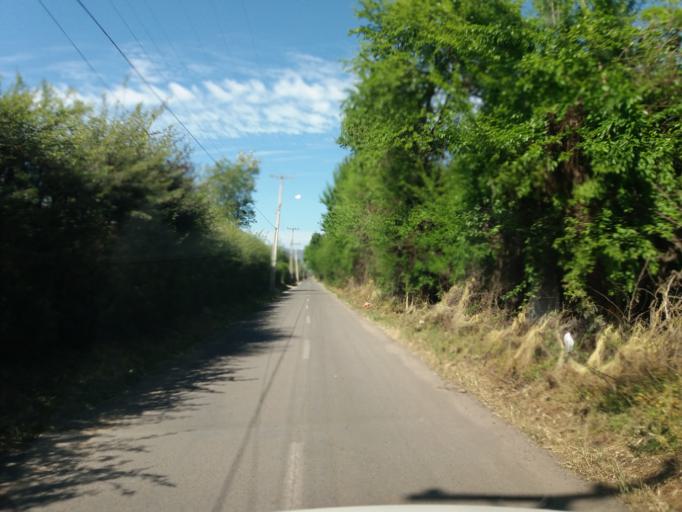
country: CL
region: Valparaiso
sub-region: Provincia de Quillota
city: Quillota
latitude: -32.8686
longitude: -71.2140
